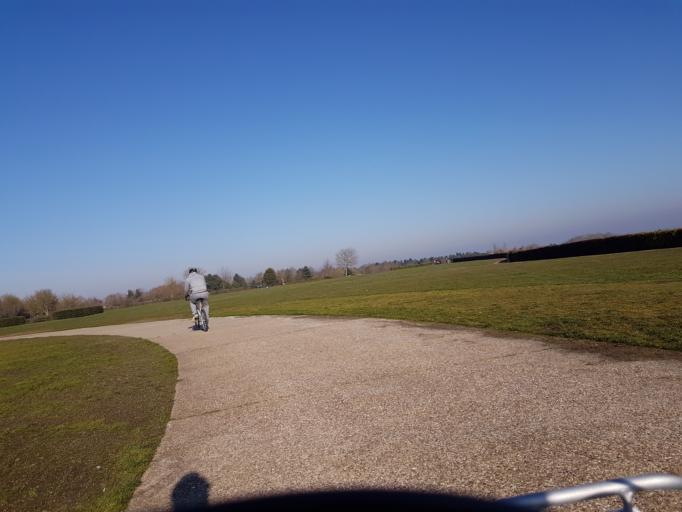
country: GB
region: England
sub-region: Milton Keynes
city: Milton Keynes
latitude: 52.0453
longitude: -0.7450
